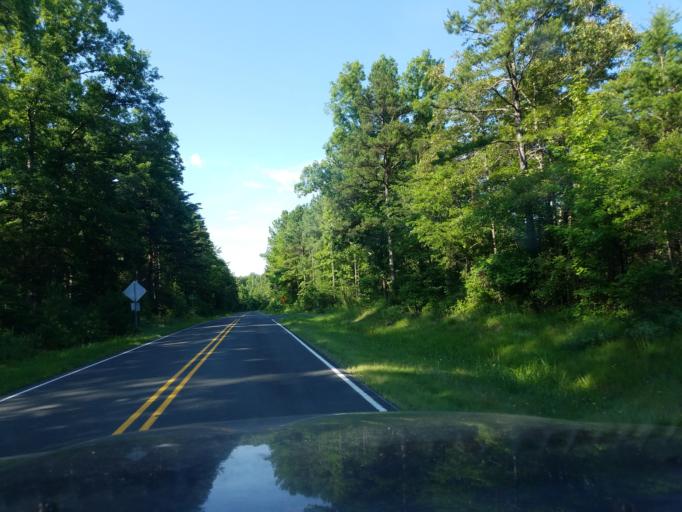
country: US
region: North Carolina
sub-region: Granville County
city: Butner
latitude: 36.1907
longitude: -78.8233
